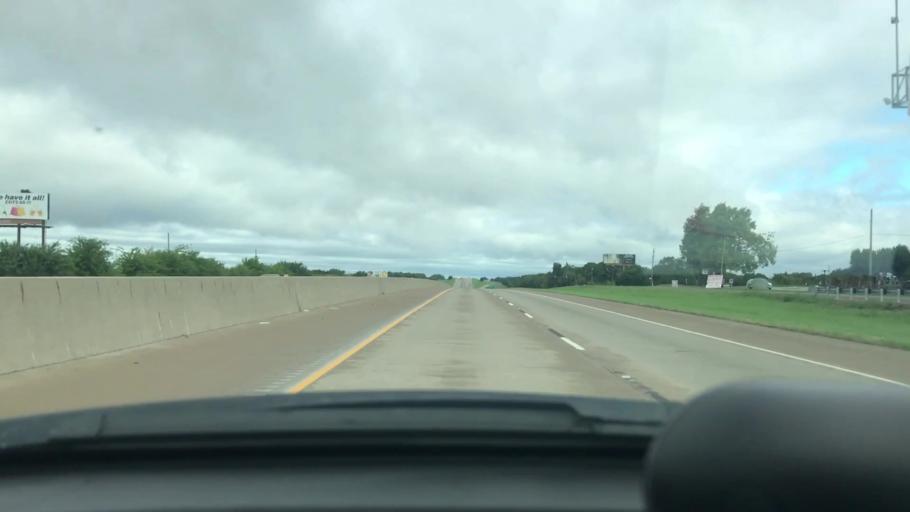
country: US
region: Texas
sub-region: Grayson County
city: Van Alstyne
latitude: 33.4514
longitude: -96.6051
